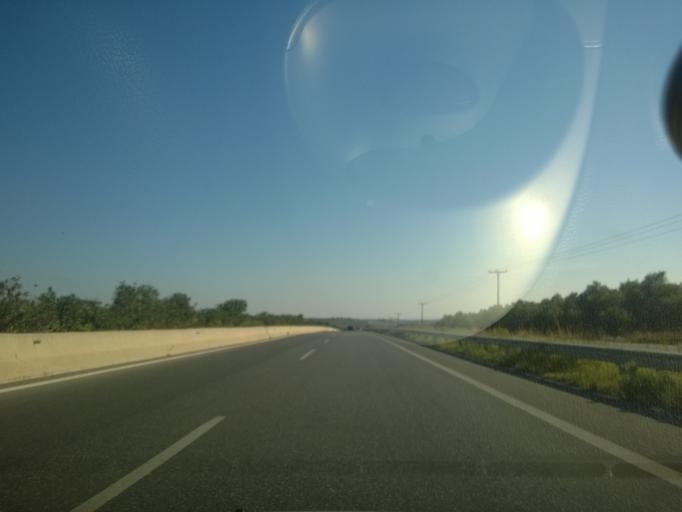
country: GR
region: Central Macedonia
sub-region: Nomos Chalkidikis
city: Lakkoma
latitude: 40.3752
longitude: 23.0428
